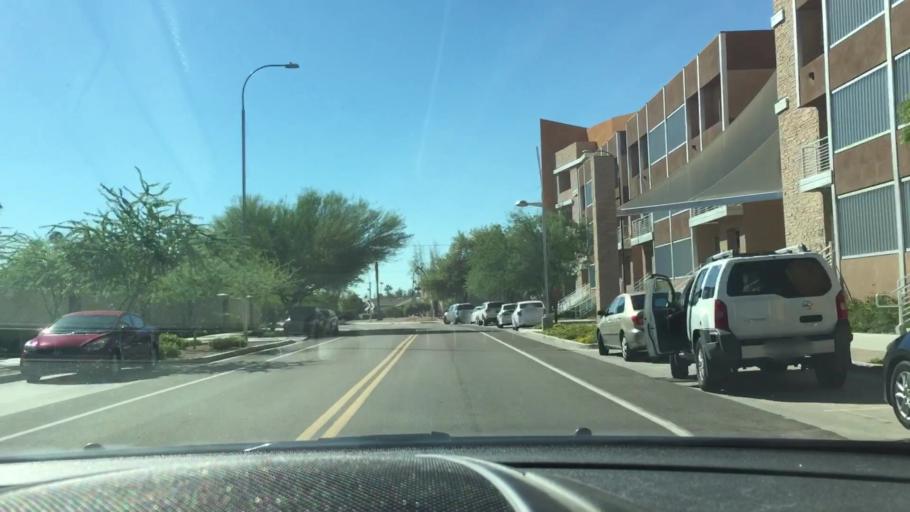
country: US
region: Arizona
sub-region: Maricopa County
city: Tempe
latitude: 33.4630
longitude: -111.9220
